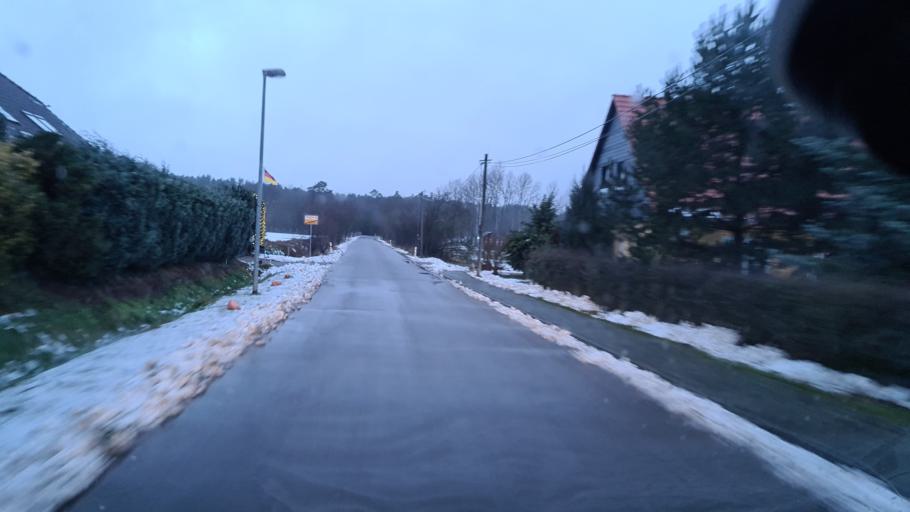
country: DE
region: Brandenburg
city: Schenkendobern
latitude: 51.9109
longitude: 14.5750
